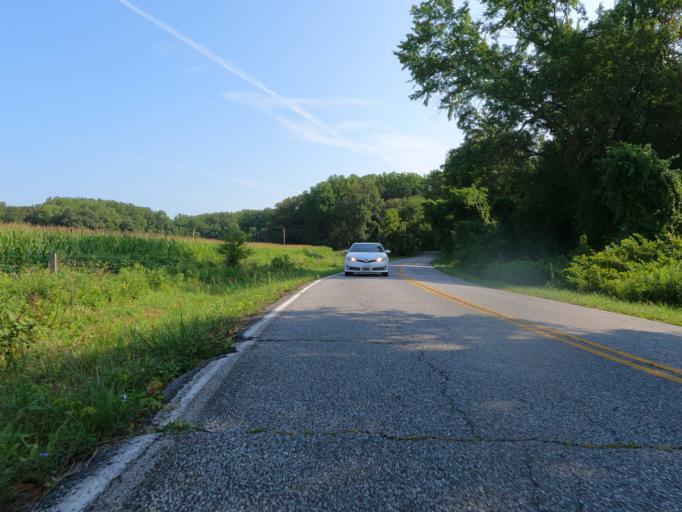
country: US
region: Maryland
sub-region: Anne Arundel County
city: Gambrills
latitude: 39.0571
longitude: -76.6611
